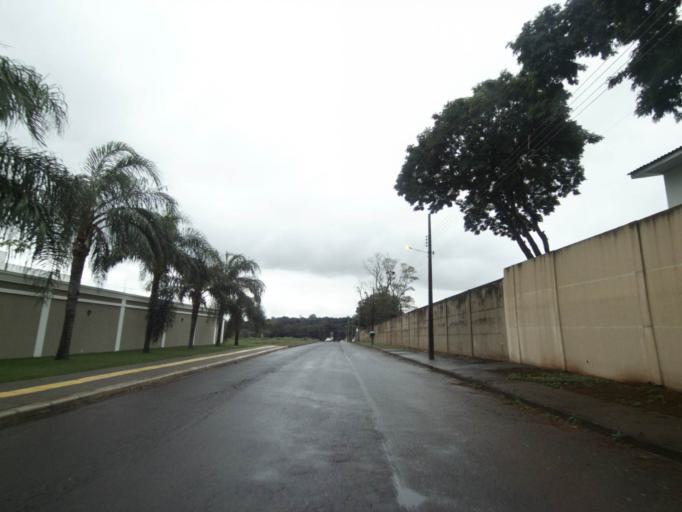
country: PY
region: Alto Parana
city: Ciudad del Este
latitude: -25.5112
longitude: -54.5804
